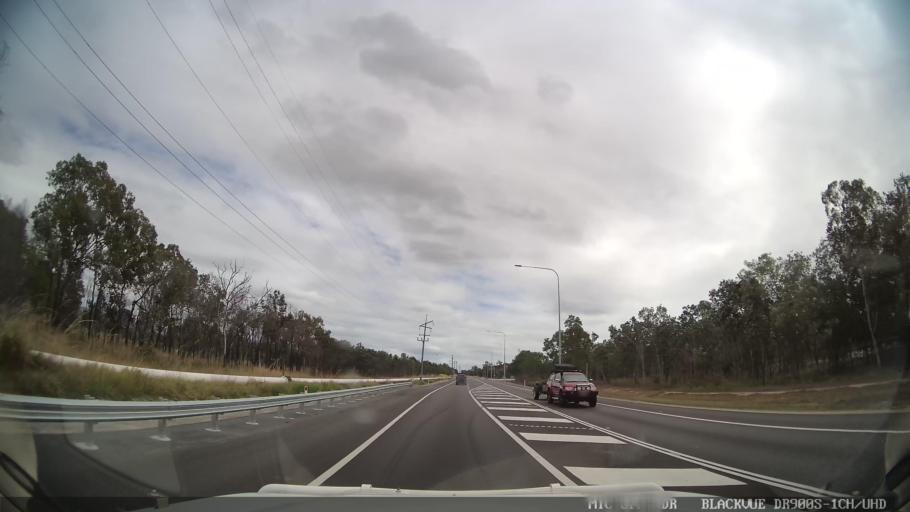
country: AU
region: Queensland
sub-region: Townsville
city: Bohle Plains
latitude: -19.1823
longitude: 146.5607
